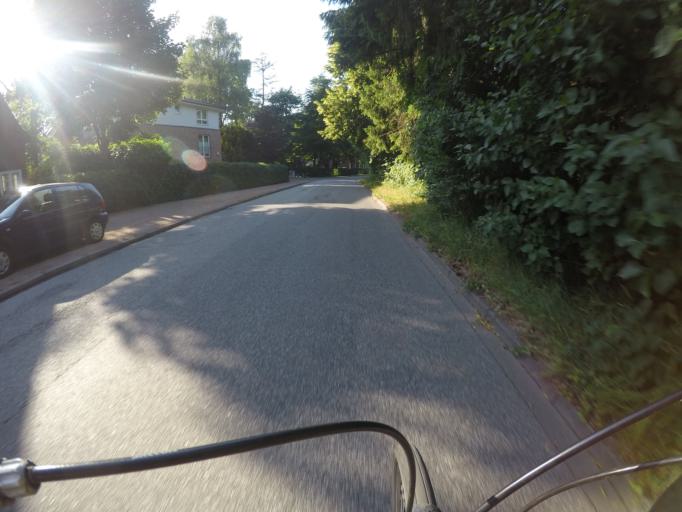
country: DE
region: Schleswig-Holstein
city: Halstenbek
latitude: 53.5689
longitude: 9.8201
